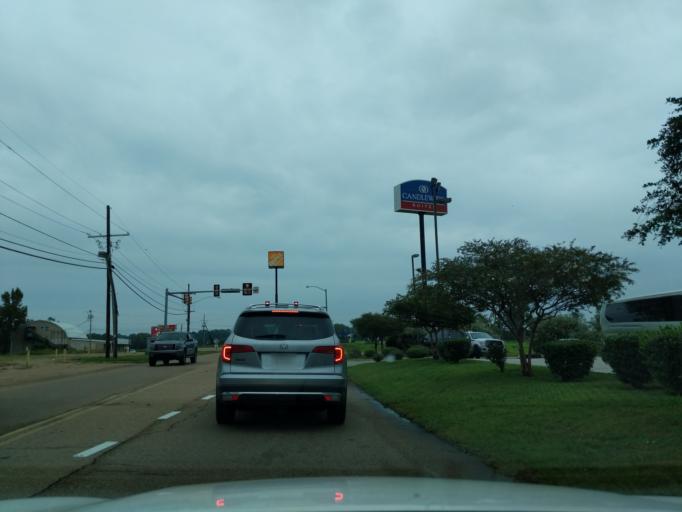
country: US
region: Mississippi
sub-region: Warren County
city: Vicksburg
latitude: 32.3166
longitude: -90.8752
